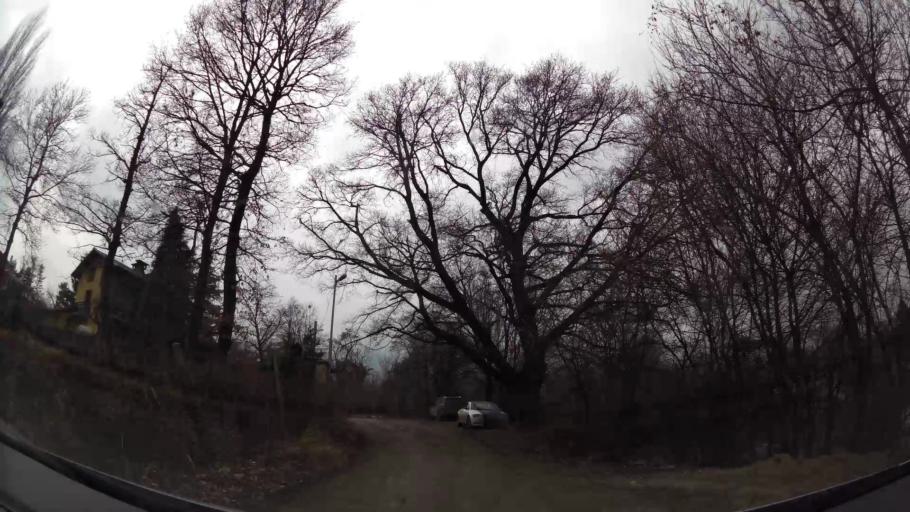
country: BG
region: Sofia-Capital
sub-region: Stolichna Obshtina
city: Sofia
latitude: 42.6176
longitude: 23.3586
